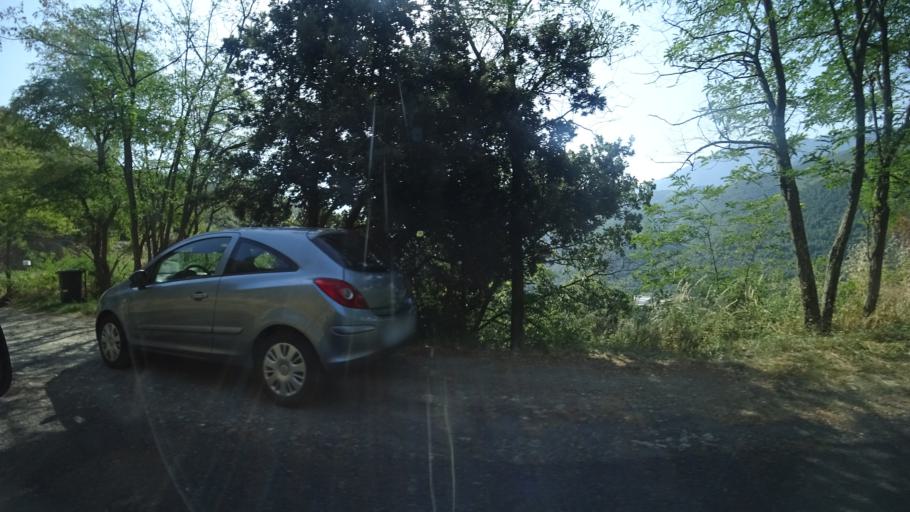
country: FR
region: Languedoc-Roussillon
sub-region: Departement des Pyrenees-Orientales
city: Vernet-les-Bains
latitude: 42.5645
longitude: 2.2879
